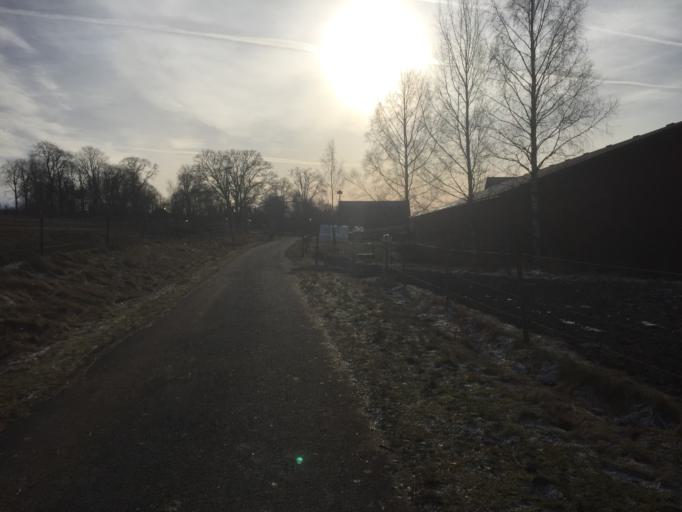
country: SE
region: Joenkoeping
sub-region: Aneby Kommun
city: Aneby
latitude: 57.8271
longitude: 14.8150
